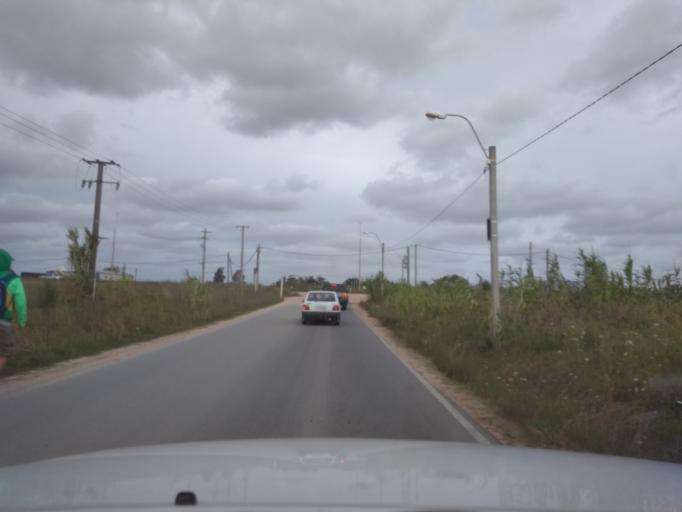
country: UY
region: Canelones
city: Colonia Nicolich
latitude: -34.7865
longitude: -56.0018
